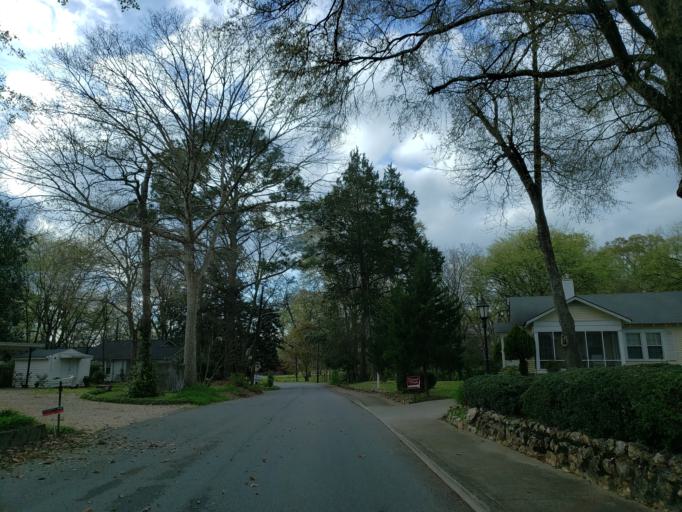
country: US
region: Georgia
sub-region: Bartow County
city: Cartersville
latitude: 34.1637
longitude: -84.8017
